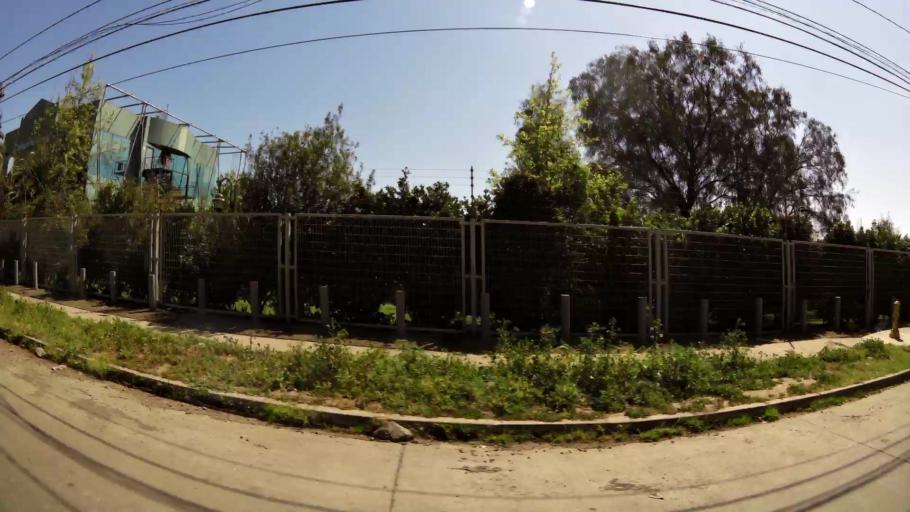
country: CL
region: Santiago Metropolitan
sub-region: Provincia de Santiago
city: Lo Prado
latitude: -33.3847
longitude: -70.7447
